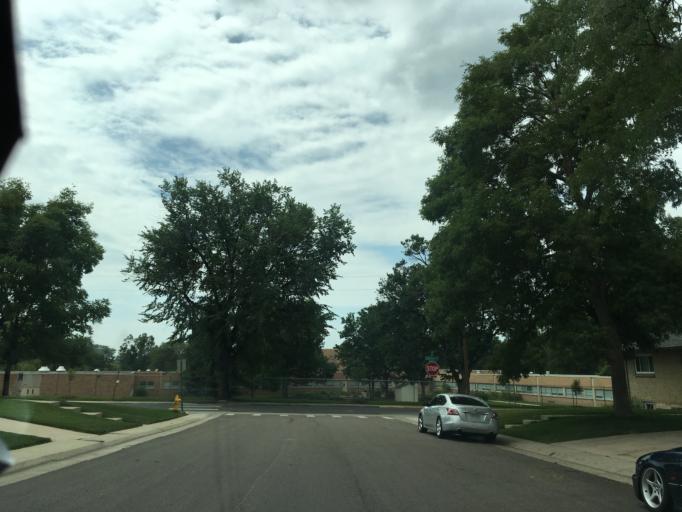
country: US
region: Colorado
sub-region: Arapahoe County
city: Sheridan
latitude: 39.6607
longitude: -105.0461
